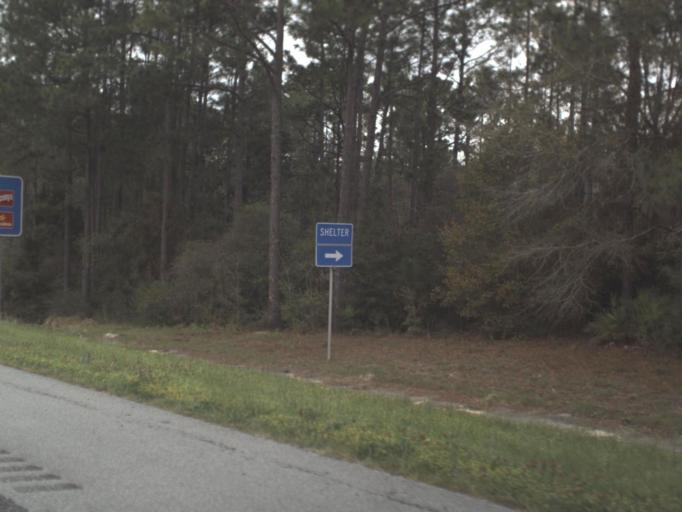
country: US
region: Florida
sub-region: Okaloosa County
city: Crestview
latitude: 30.7268
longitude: -86.5558
